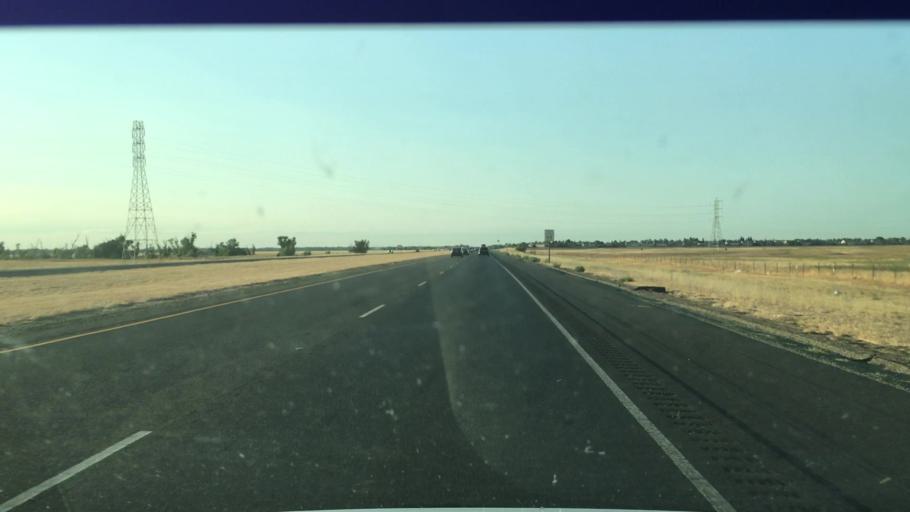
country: US
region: California
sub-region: Sacramento County
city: Laguna
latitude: 38.3842
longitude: -121.4784
